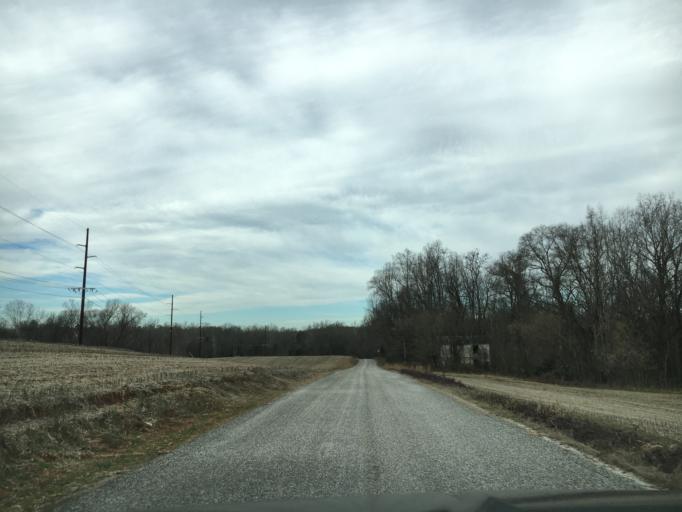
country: US
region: Virginia
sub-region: Powhatan County
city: Powhatan
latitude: 37.4794
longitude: -77.9676
